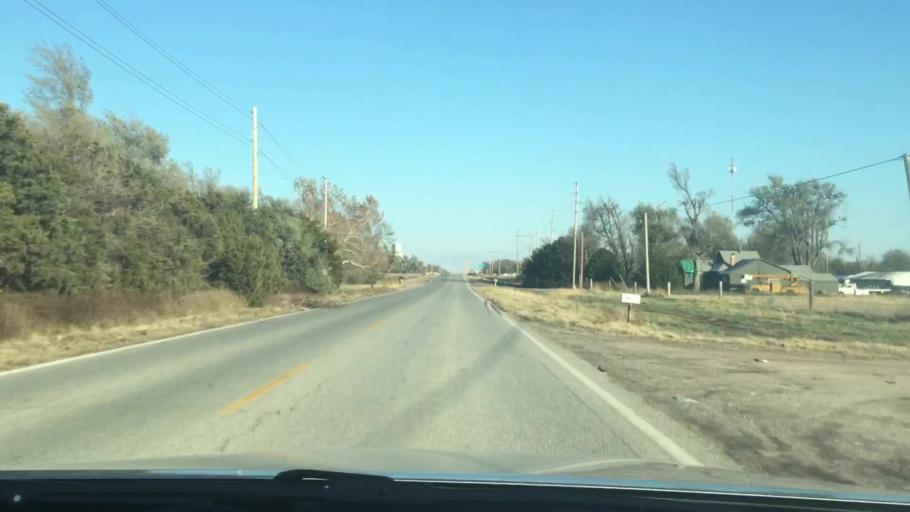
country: US
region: Kansas
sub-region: Reno County
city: Hutchinson
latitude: 38.0572
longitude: -97.9706
